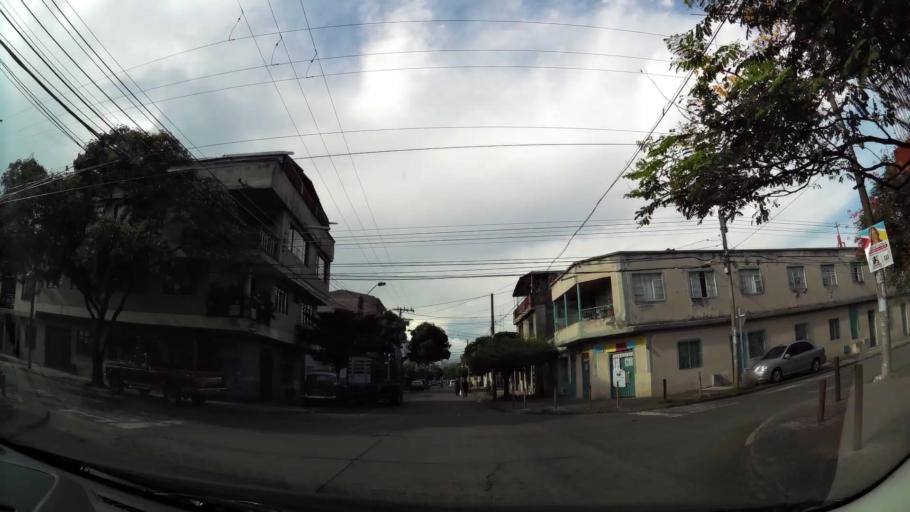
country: CO
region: Valle del Cauca
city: Cali
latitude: 3.4232
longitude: -76.5267
